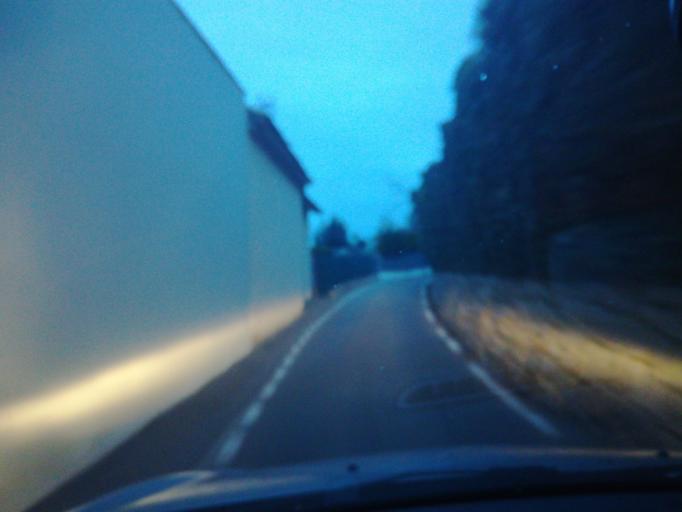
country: FR
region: Provence-Alpes-Cote d'Azur
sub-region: Departement des Alpes-Maritimes
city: Mougins
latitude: 43.6083
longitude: 7.0010
